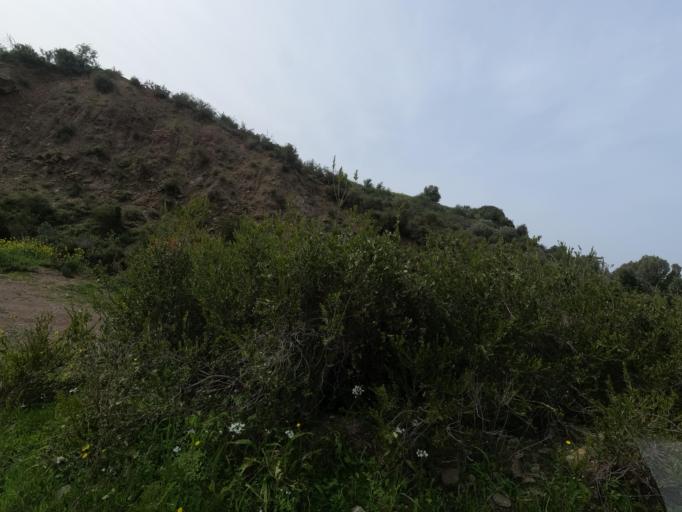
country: CY
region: Pafos
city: Pegeia
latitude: 34.9489
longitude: 32.3575
